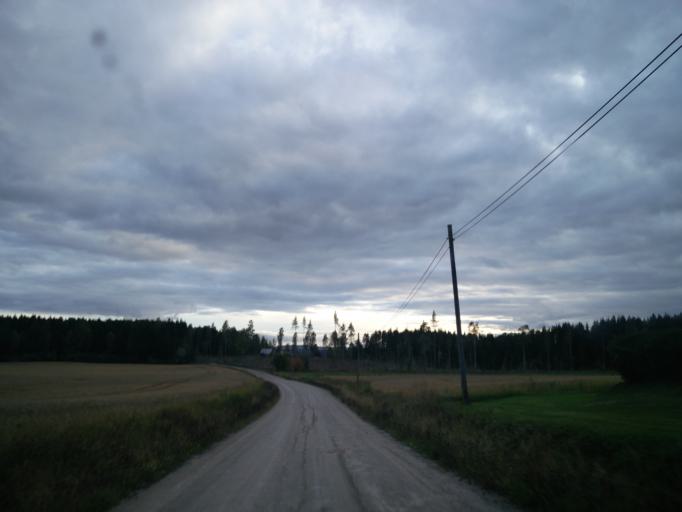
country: SE
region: Vaesternorrland
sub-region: Sundsvalls Kommun
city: Matfors
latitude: 62.3407
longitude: 17.0713
